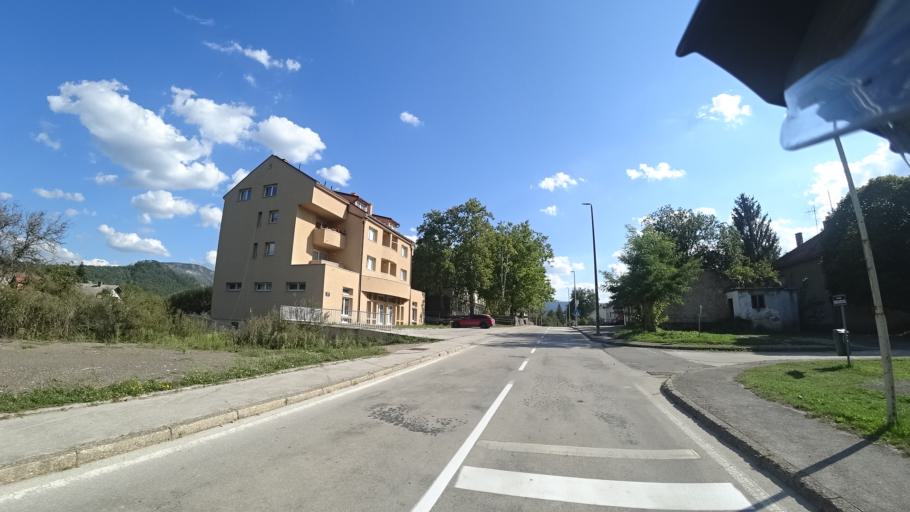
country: BA
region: Federation of Bosnia and Herzegovina
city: Orasac
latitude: 44.3649
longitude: 16.1241
